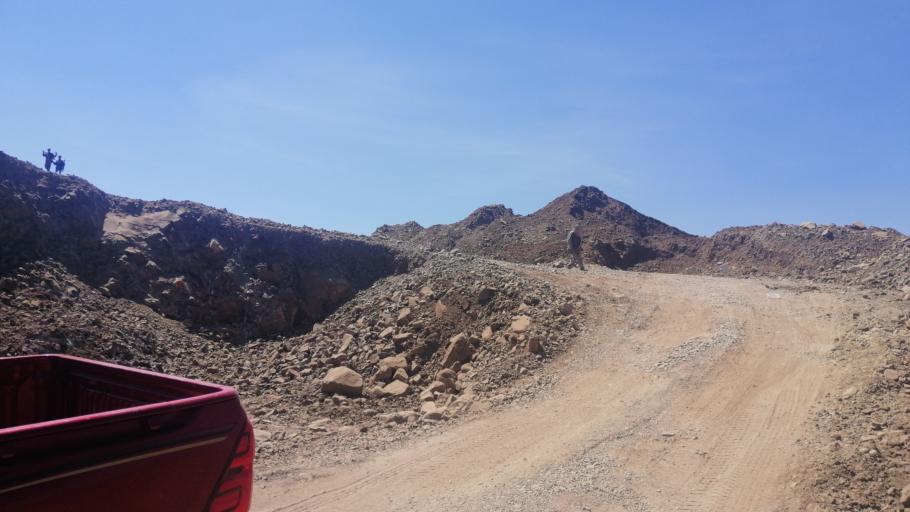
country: ET
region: Amhara
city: Debre Tabor
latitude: 11.4226
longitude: 38.1415
